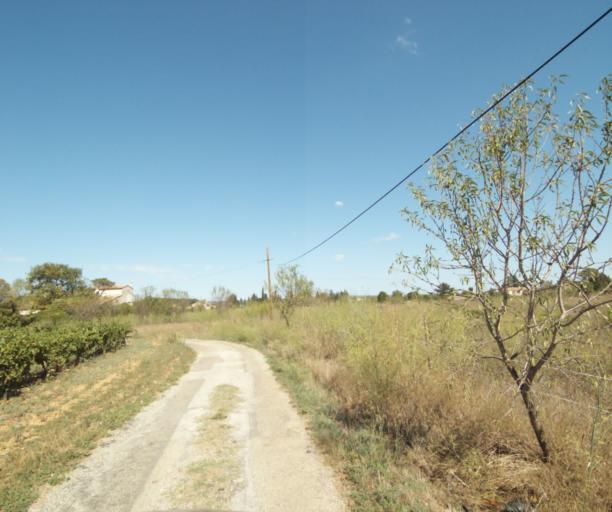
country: FR
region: Languedoc-Roussillon
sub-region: Departement du Gard
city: Rodilhan
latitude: 43.8198
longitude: 4.4349
